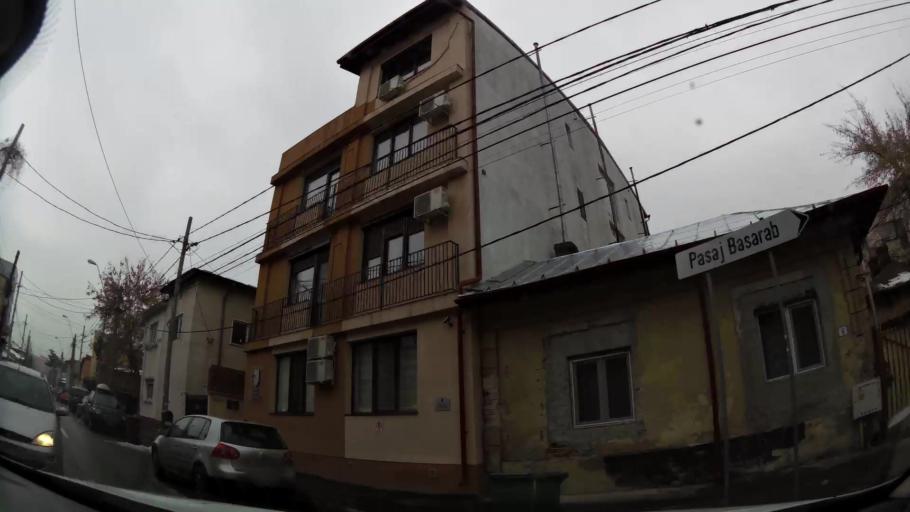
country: RO
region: Bucuresti
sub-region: Municipiul Bucuresti
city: Bucuresti
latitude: 44.4528
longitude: 26.0714
